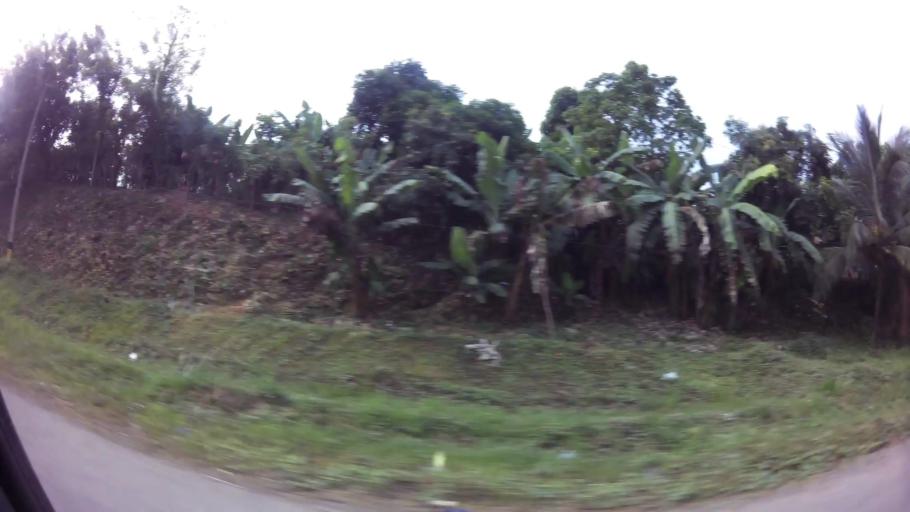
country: HN
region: Yoro
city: Guaimitas
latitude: 15.5112
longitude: -87.6791
